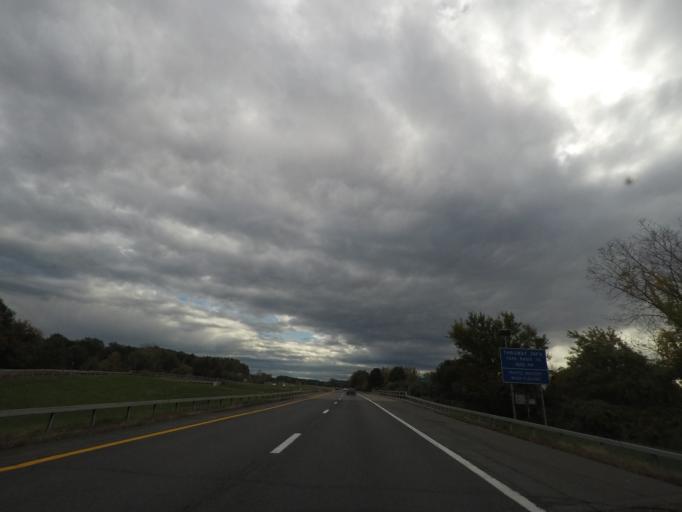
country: US
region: New York
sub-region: Rensselaer County
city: Castleton-on-Hudson
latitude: 42.5133
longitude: -73.6894
